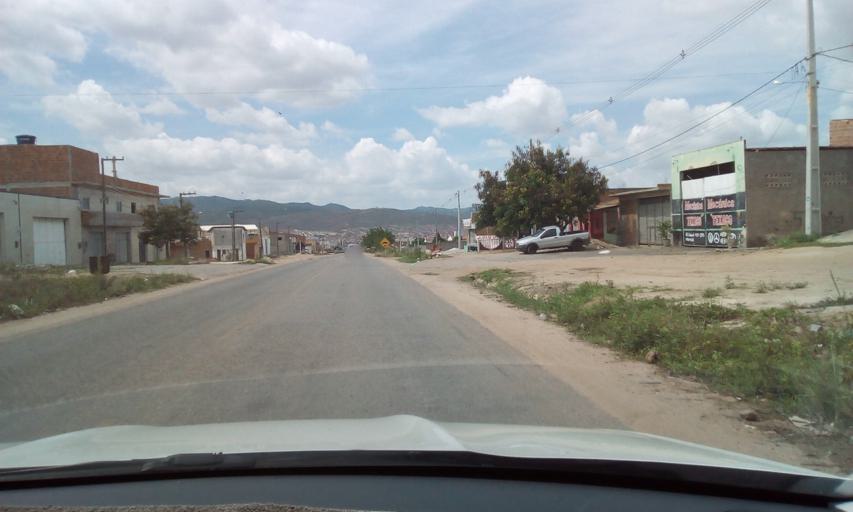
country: BR
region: Pernambuco
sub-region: Bezerros
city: Bezerros
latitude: -8.2548
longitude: -35.7577
